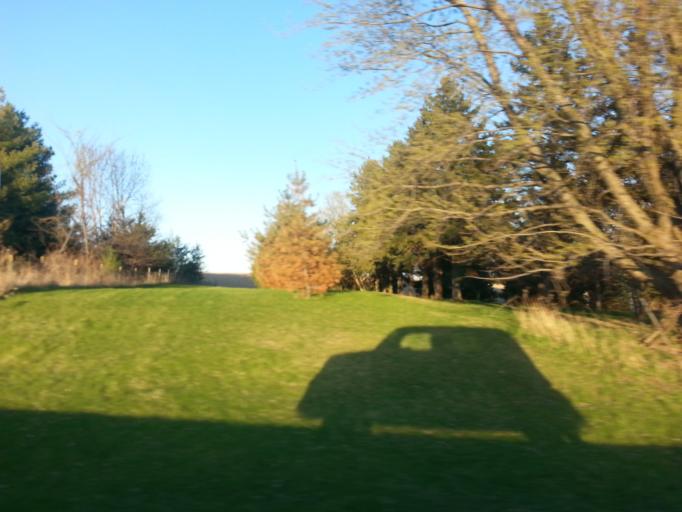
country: US
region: Wisconsin
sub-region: Pierce County
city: Prescott
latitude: 44.7766
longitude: -92.8174
